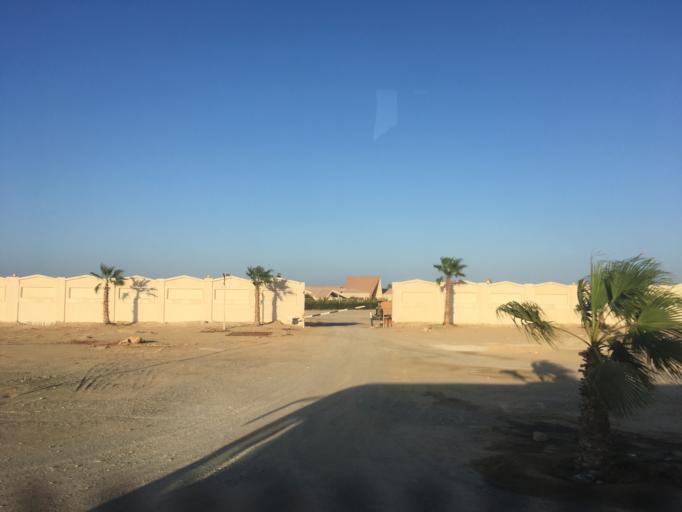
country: EG
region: Red Sea
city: Al Qusayr
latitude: 25.9656
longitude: 34.3586
